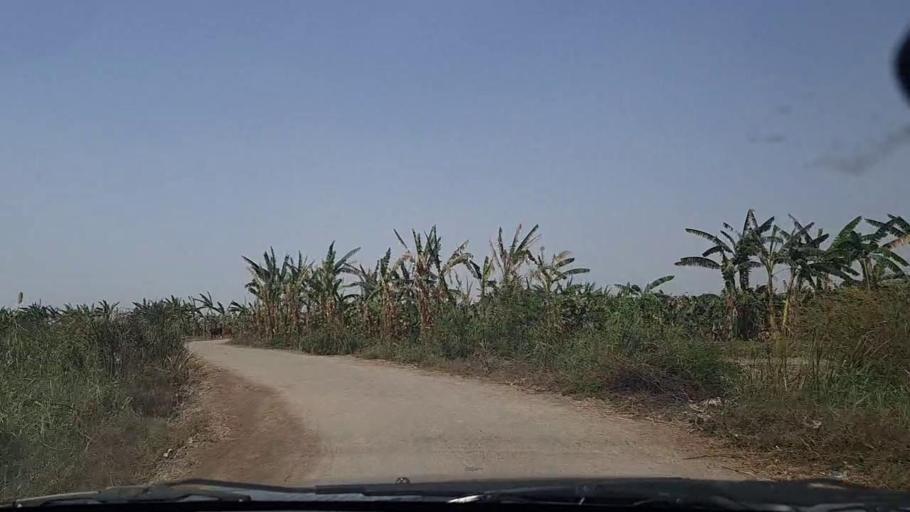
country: PK
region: Sindh
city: Keti Bandar
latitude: 24.2787
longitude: 67.6714
